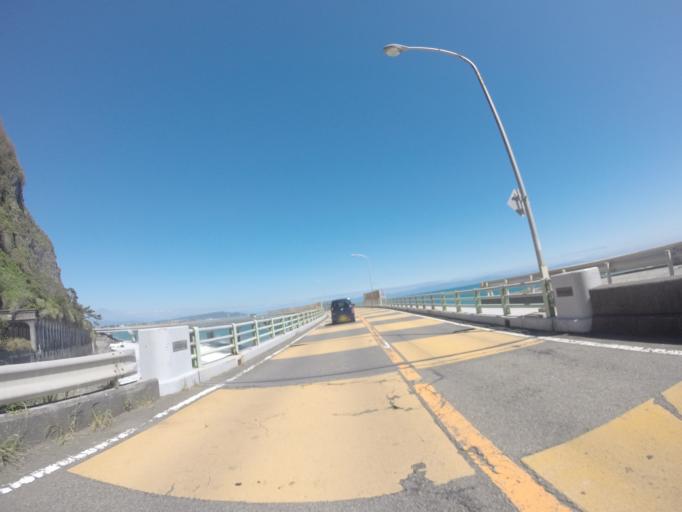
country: JP
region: Shizuoka
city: Yaizu
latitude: 34.9058
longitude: 138.3517
